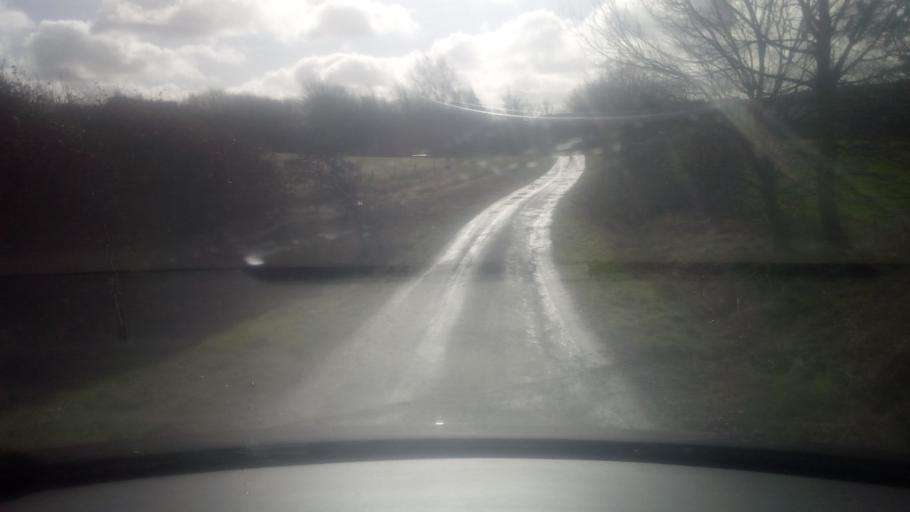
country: GB
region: Scotland
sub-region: The Scottish Borders
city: Jedburgh
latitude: 55.5191
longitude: -2.5712
